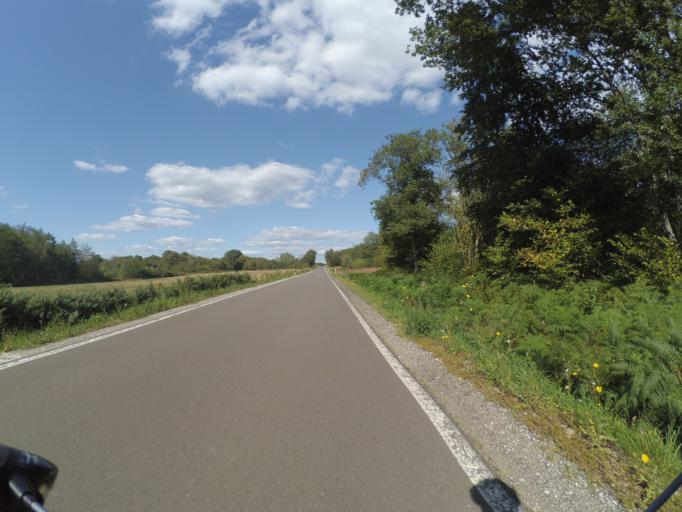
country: DE
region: Rheinland-Pfalz
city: Polich
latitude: 49.7681
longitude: 6.8478
